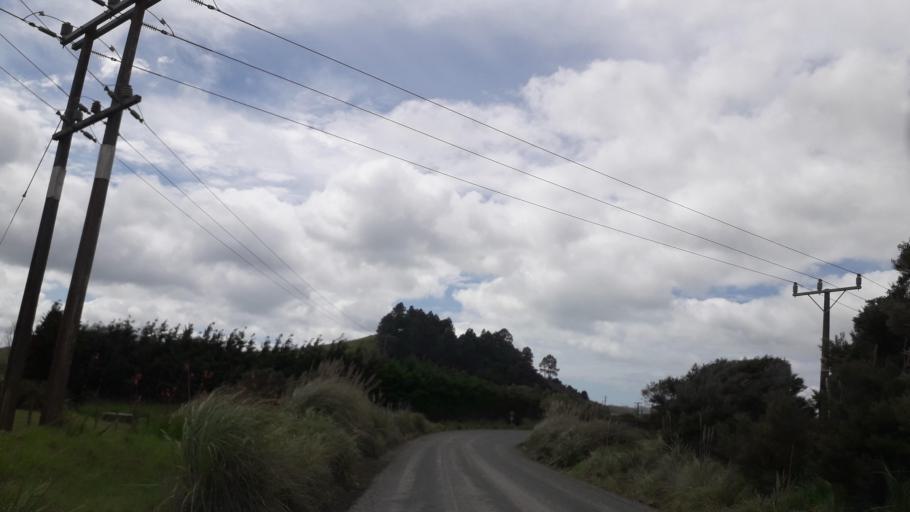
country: NZ
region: Northland
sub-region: Far North District
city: Taipa
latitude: -35.0110
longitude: 173.4258
